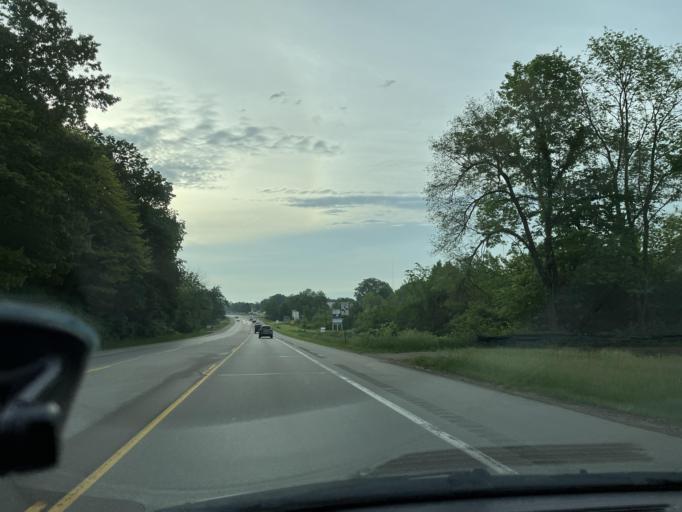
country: US
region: Michigan
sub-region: Barry County
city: Hastings
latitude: 42.6457
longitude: -85.3288
